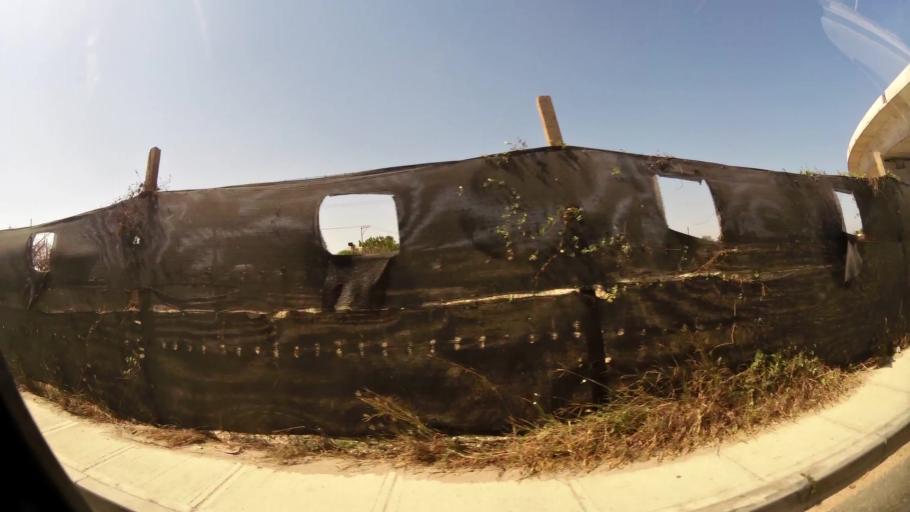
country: CO
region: Atlantico
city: Barranquilla
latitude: 10.9508
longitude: -74.7674
